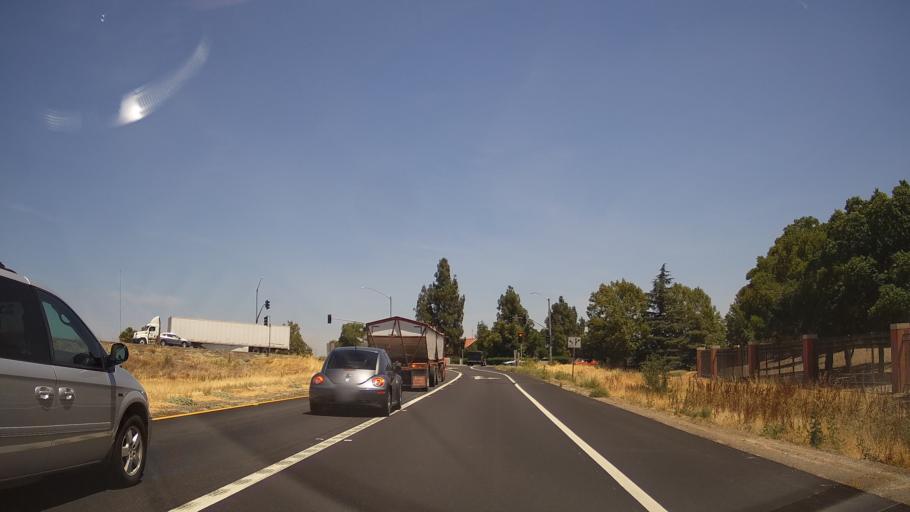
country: US
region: California
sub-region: Solano County
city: Hartley
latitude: 38.3929
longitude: -121.9484
